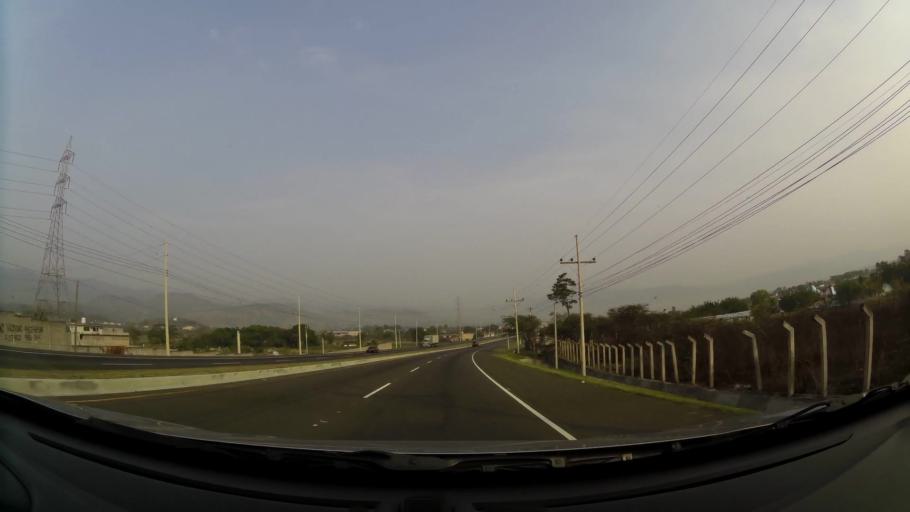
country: HN
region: Francisco Morazan
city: Tamara
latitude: 14.1986
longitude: -87.3424
